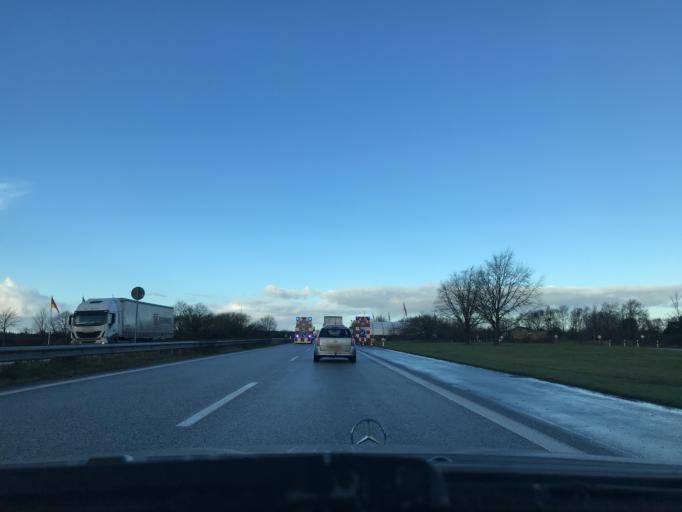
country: DE
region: Schleswig-Holstein
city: Handewitt
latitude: 54.8047
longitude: 9.3290
